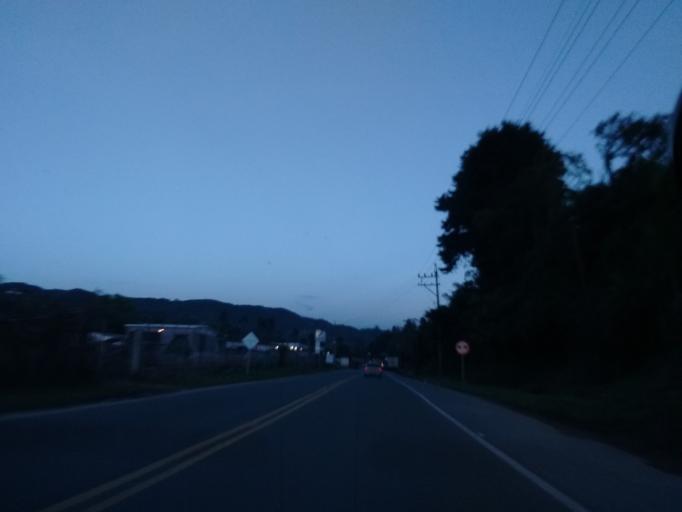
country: CO
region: Antioquia
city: Santuario
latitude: 6.1291
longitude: -75.2545
